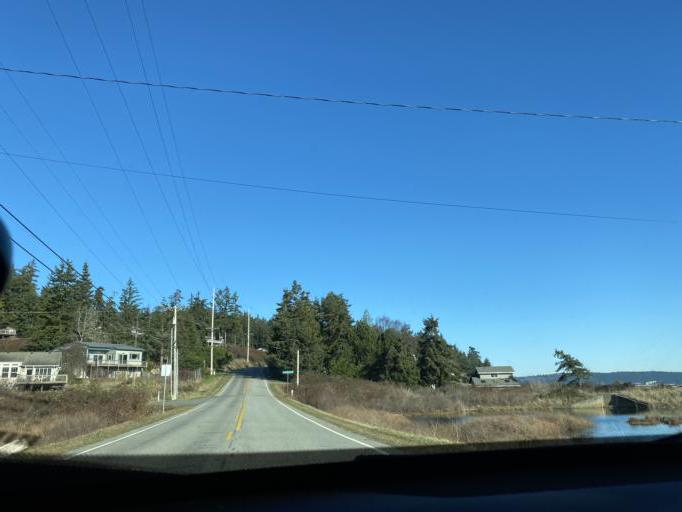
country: US
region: Washington
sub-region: Island County
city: Camano
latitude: 48.1097
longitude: -122.5683
